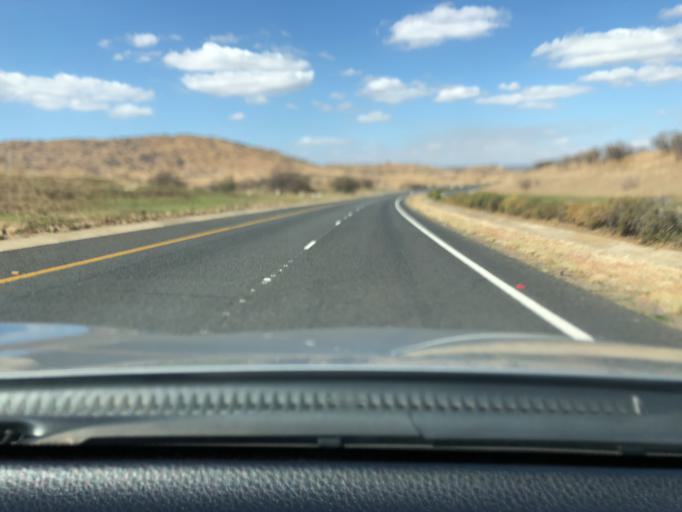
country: ZA
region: KwaZulu-Natal
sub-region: uThukela District Municipality
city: Ladysmith
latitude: -28.6689
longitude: 29.6346
